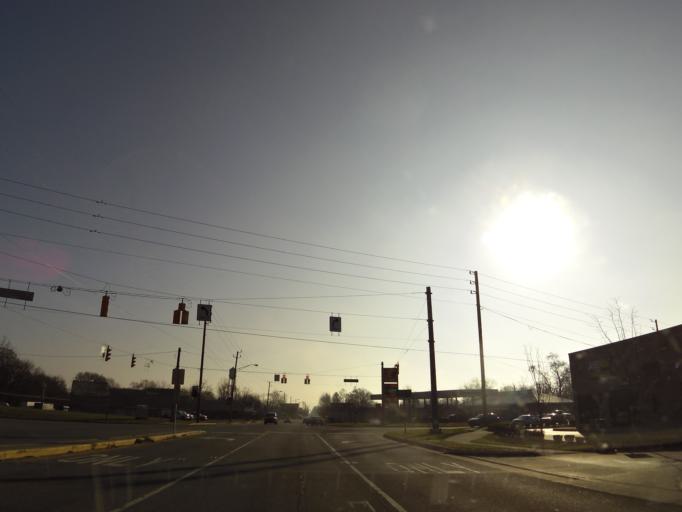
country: US
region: Indiana
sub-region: Marion County
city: Clermont
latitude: 39.8178
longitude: -86.3277
